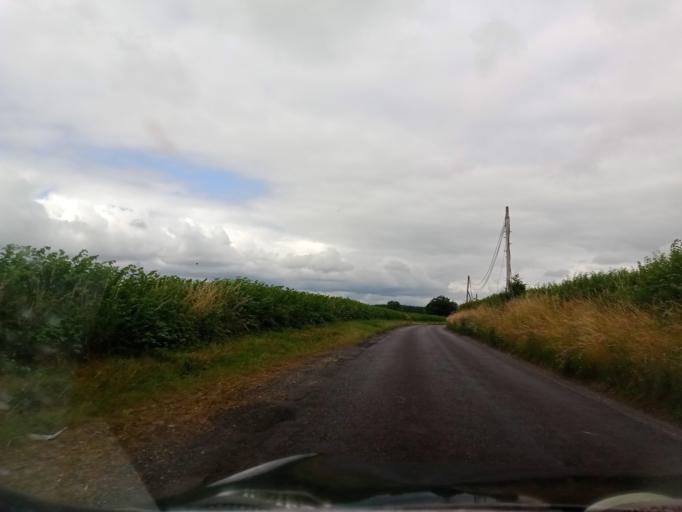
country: IE
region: Leinster
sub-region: Laois
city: Stradbally
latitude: 52.9897
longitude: -7.1808
